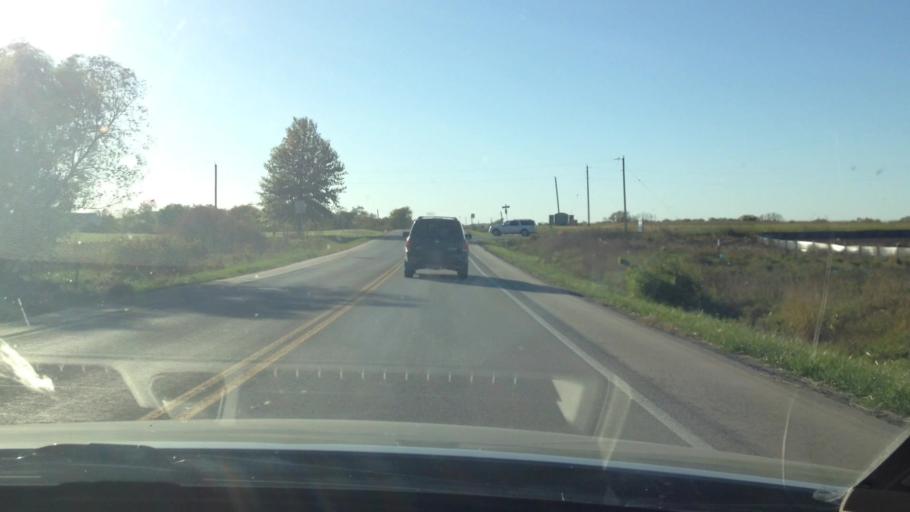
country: US
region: Kansas
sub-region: Johnson County
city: Edgerton
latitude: 38.7676
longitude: -94.9722
